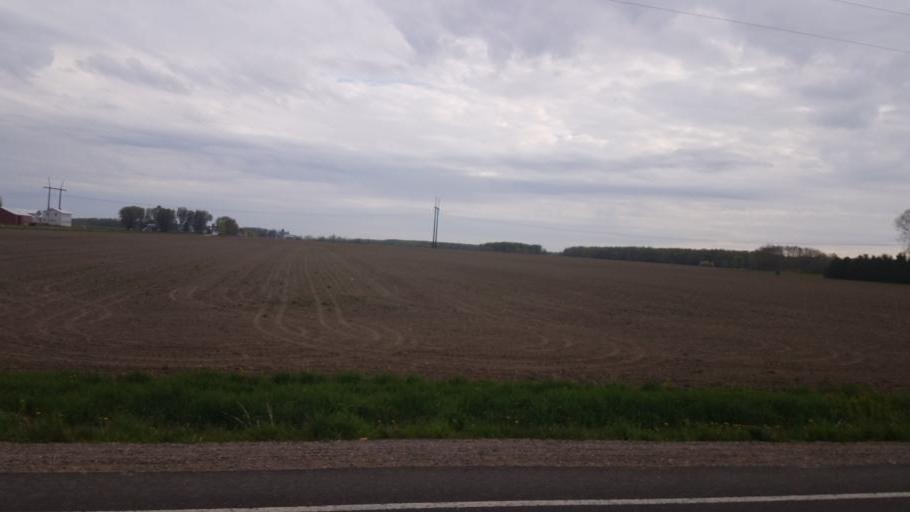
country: US
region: Wisconsin
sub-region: Marathon County
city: Spencer
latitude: 44.6552
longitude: -90.3765
